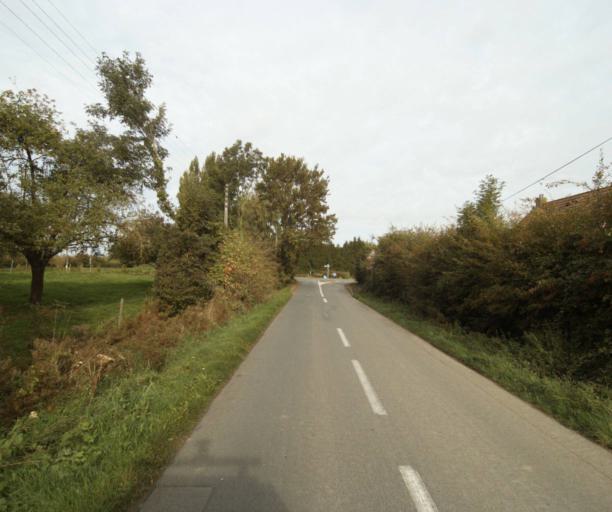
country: FR
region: Nord-Pas-de-Calais
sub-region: Departement du Nord
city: Herlies
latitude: 50.6042
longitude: 2.8533
